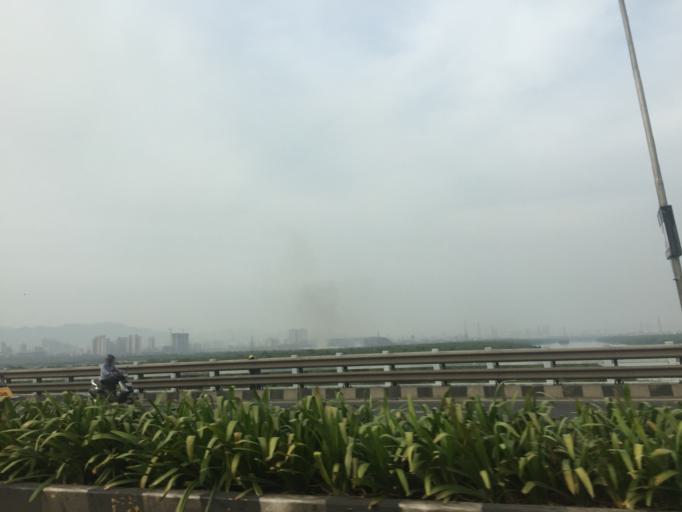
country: IN
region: Maharashtra
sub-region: Thane
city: Airoli
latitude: 19.1511
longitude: 72.9785
